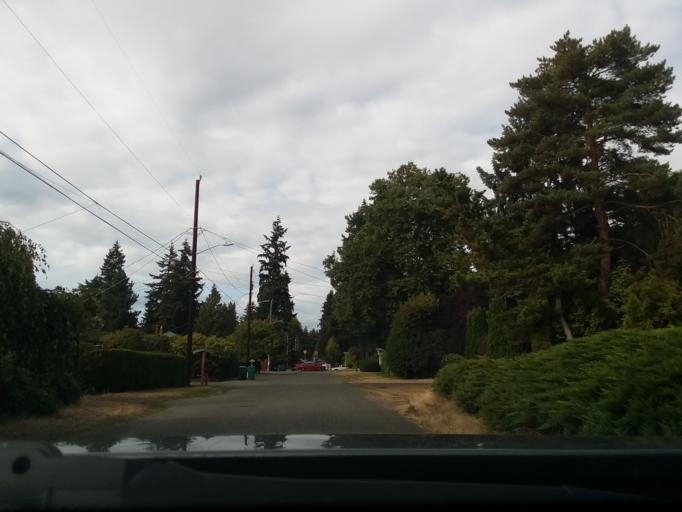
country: US
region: Washington
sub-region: King County
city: Shoreline
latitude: 47.7206
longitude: -122.3623
